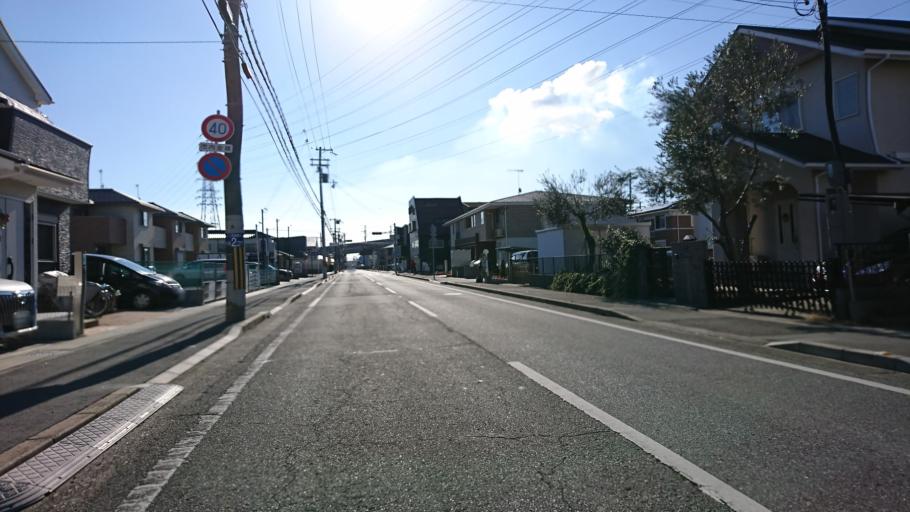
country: JP
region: Hyogo
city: Kakogawacho-honmachi
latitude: 34.7372
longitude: 134.8429
